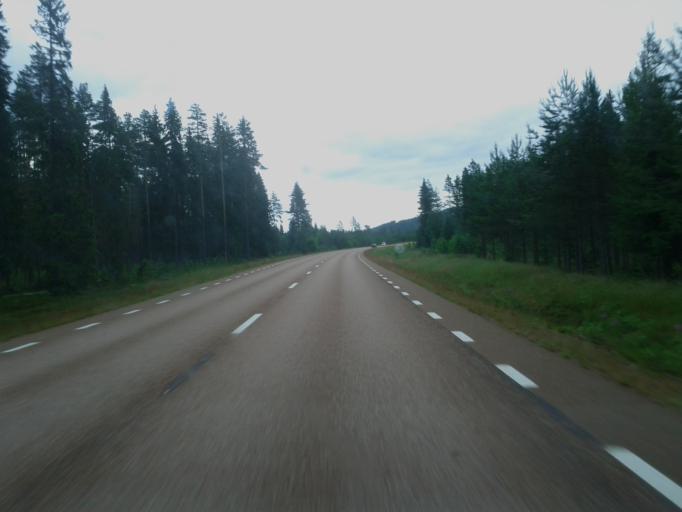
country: SE
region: Dalarna
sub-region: Alvdalens Kommun
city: AElvdalen
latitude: 61.2778
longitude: 13.8811
